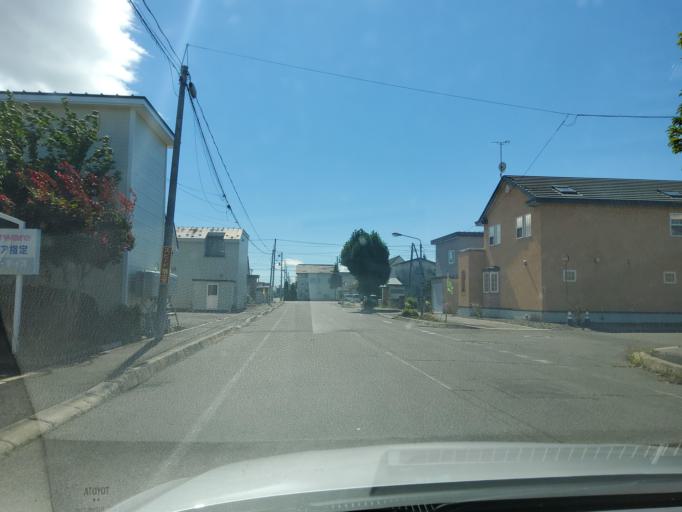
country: JP
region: Hokkaido
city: Otofuke
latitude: 42.9574
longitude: 143.1939
